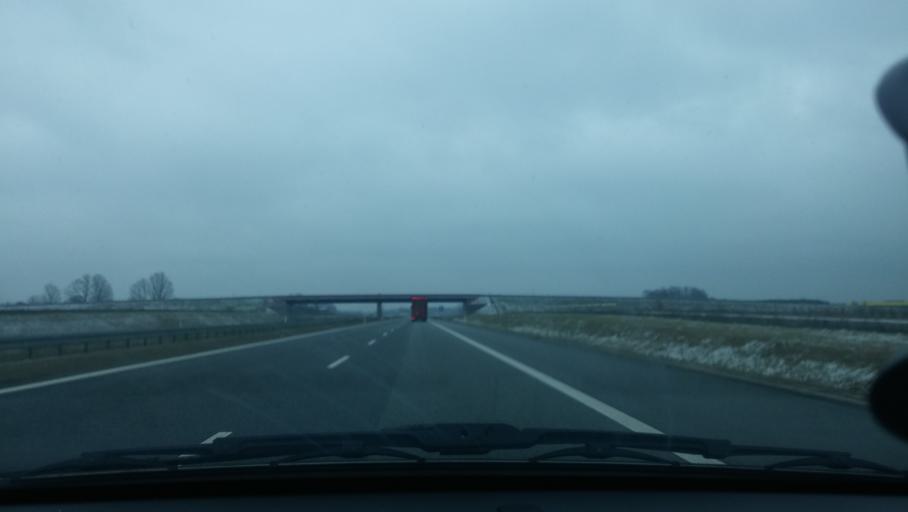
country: PL
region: Masovian Voivodeship
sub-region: Powiat minski
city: Jakubow
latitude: 52.2038
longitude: 21.6974
